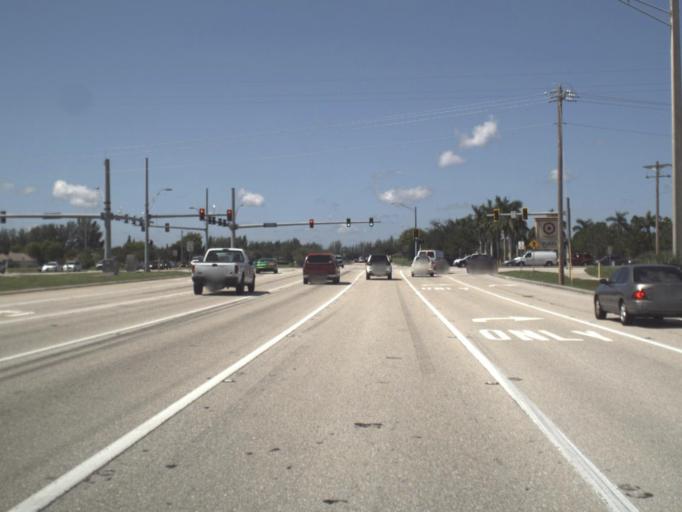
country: US
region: Florida
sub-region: Lee County
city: Cape Coral
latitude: 26.6046
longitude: -81.9730
